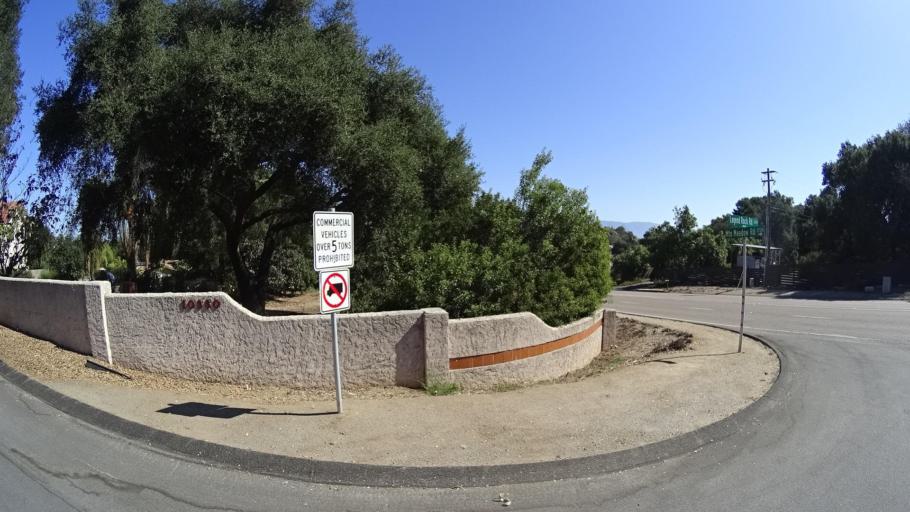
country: US
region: California
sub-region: San Diego County
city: Hidden Meadows
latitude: 33.2082
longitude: -117.1098
